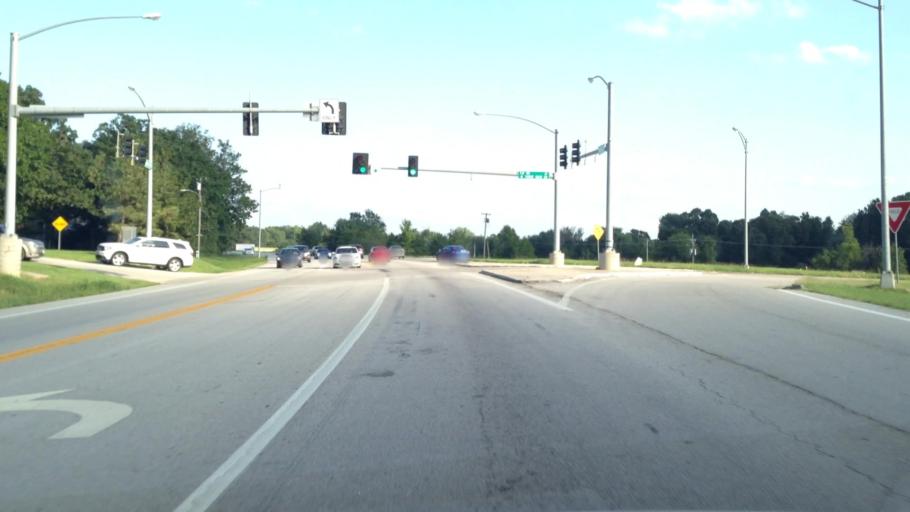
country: US
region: Missouri
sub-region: Jasper County
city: Carl Junction
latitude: 37.1446
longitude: -94.5219
